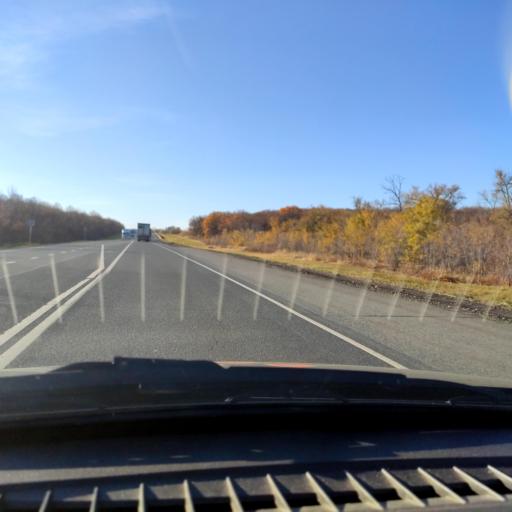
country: RU
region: Samara
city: Mezhdurechensk
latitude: 53.2586
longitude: 49.0965
